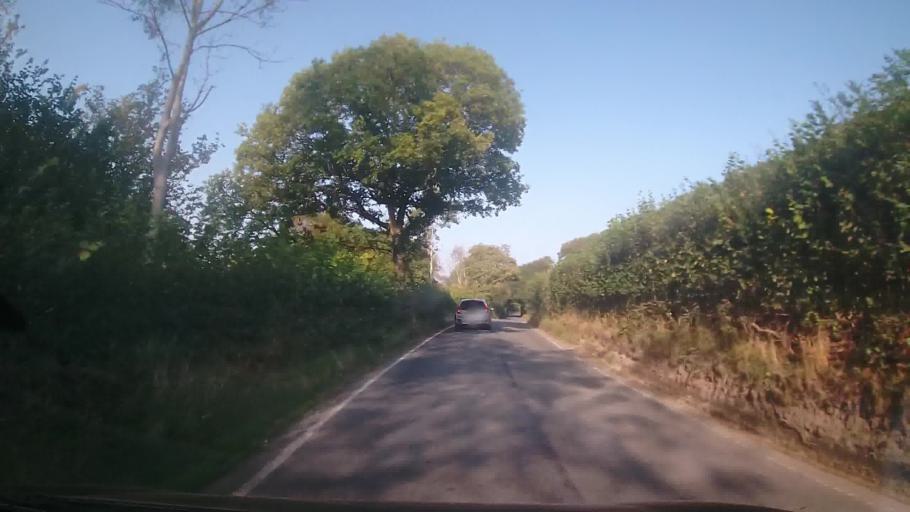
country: GB
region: Wales
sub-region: County of Ceredigion
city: Lledrod
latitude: 52.2510
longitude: -3.9115
